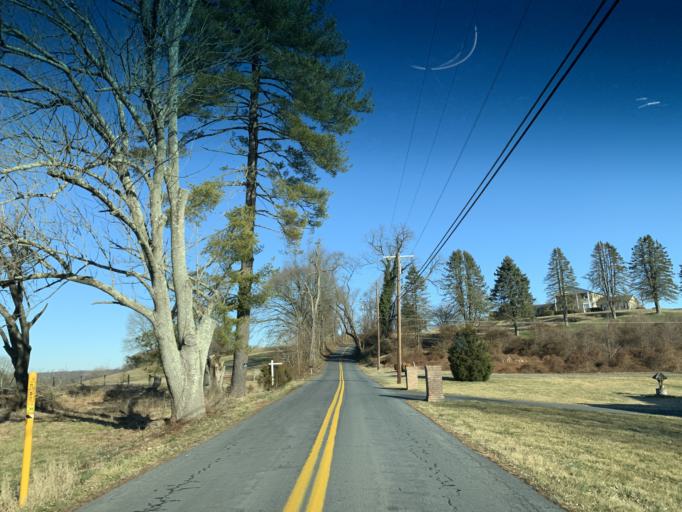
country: US
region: Maryland
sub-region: Harford County
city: Aberdeen
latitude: 39.5972
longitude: -76.2249
